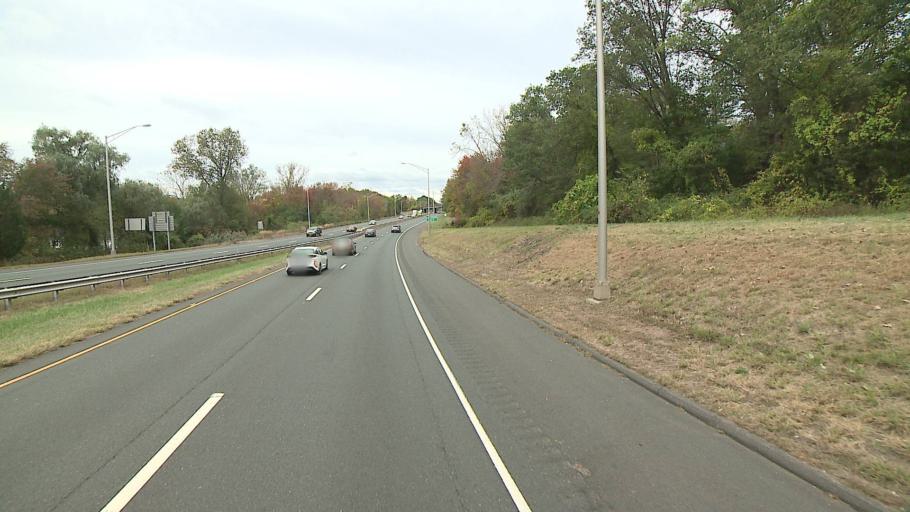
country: US
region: Connecticut
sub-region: Middlesex County
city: Middletown
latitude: 41.5394
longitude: -72.6241
